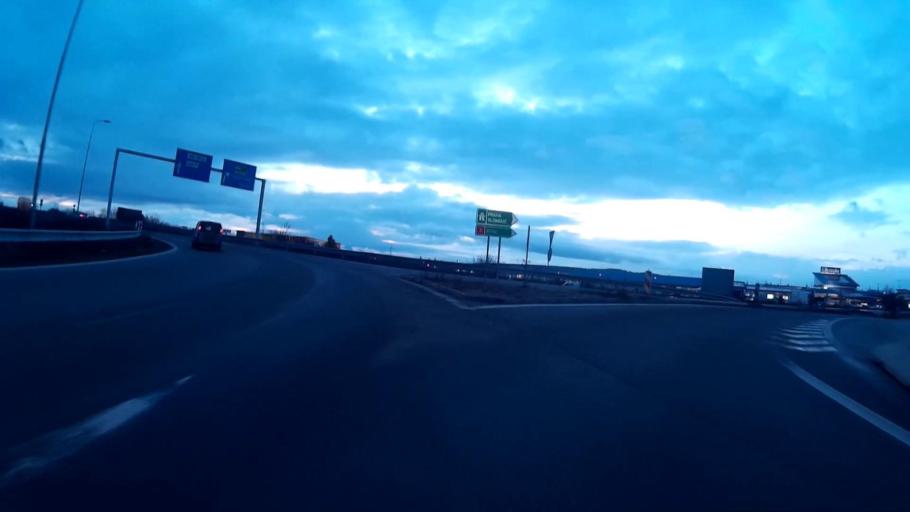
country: CZ
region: South Moravian
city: Modrice
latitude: 49.1360
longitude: 16.6387
